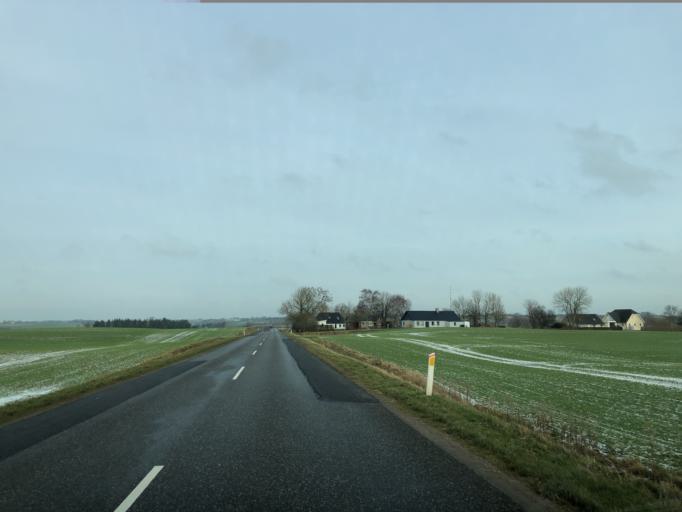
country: DK
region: South Denmark
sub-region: Vejle Kommune
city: Jelling
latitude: 55.7940
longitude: 9.4472
